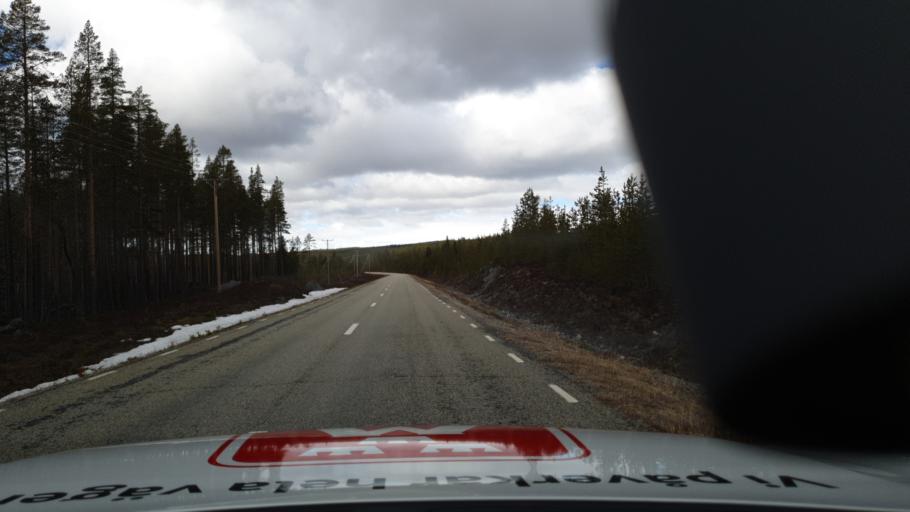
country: SE
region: Jaemtland
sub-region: Are Kommun
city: Jarpen
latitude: 62.8055
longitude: 13.6623
